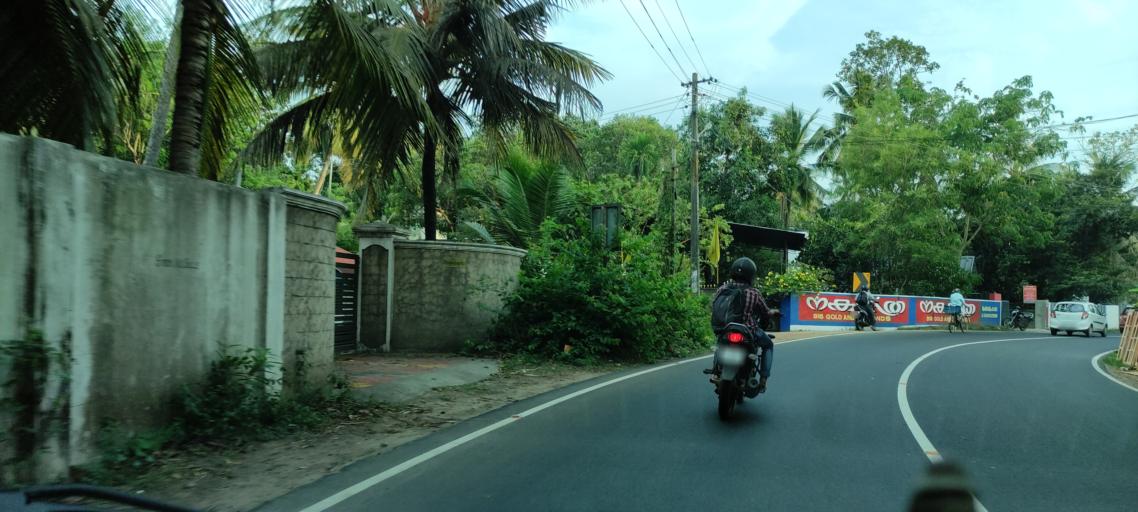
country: IN
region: Kerala
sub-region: Alappuzha
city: Arukutti
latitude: 9.8642
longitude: 76.3241
